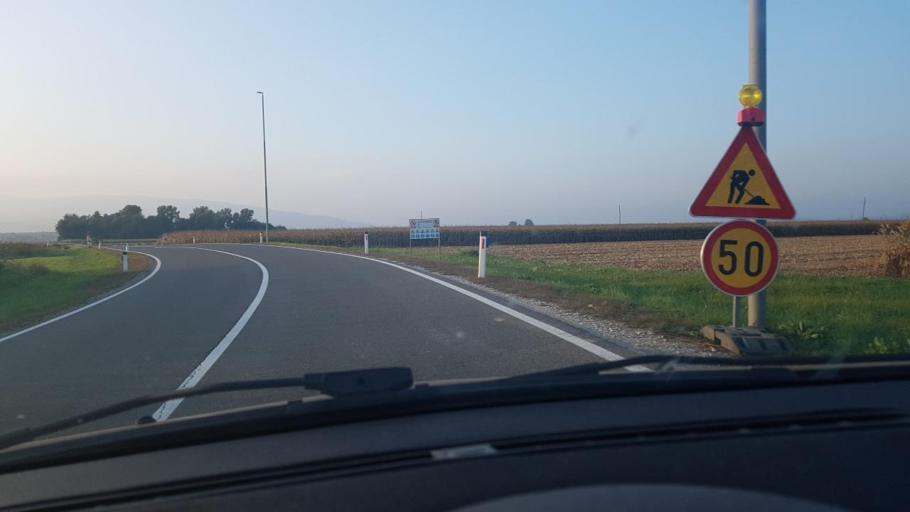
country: SI
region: Race-Fram
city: Race
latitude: 46.4092
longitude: 15.7111
